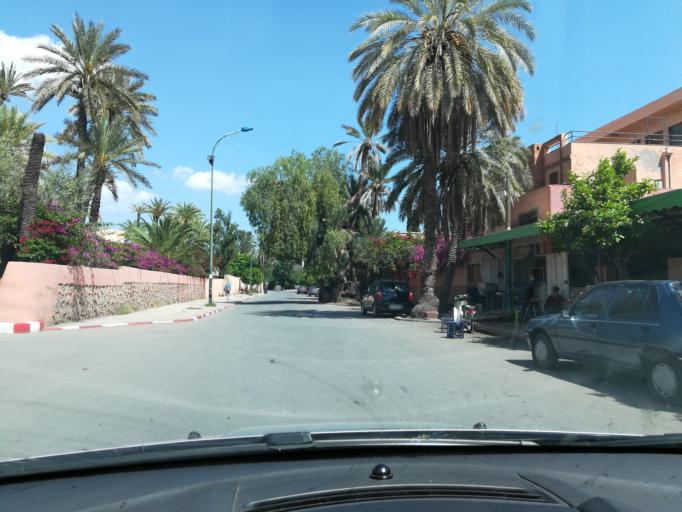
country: MA
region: Marrakech-Tensift-Al Haouz
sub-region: Marrakech
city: Marrakesh
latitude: 31.6405
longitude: -8.0144
